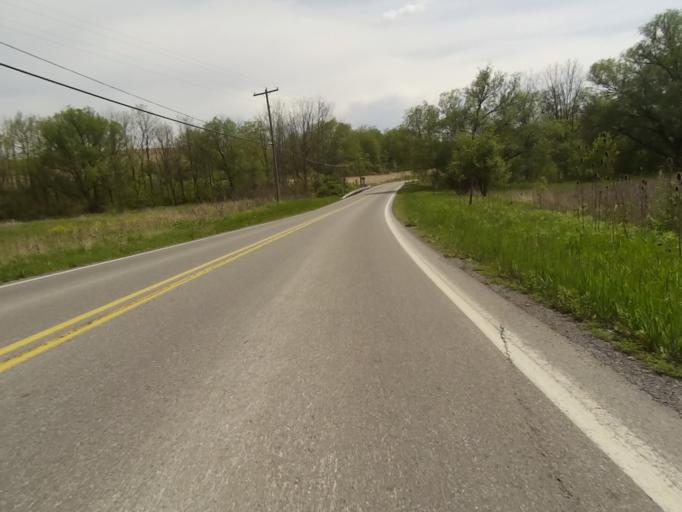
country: US
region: Pennsylvania
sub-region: Centre County
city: Zion
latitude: 40.9956
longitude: -77.6399
